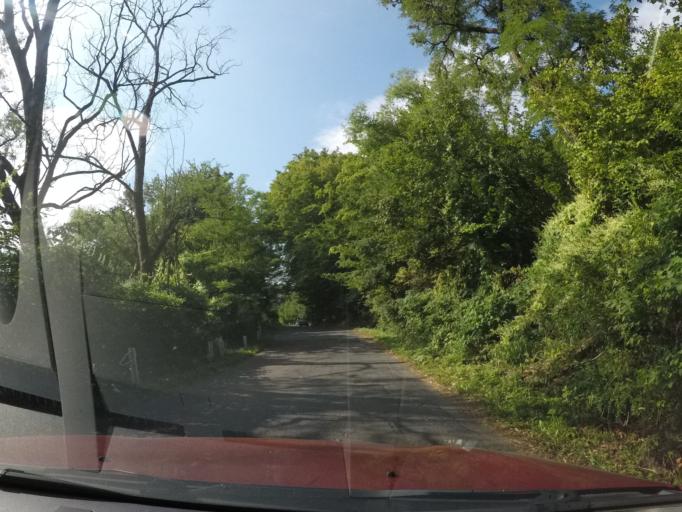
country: UA
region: Zakarpattia
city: Velykyi Bereznyi
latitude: 48.9156
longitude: 22.4591
